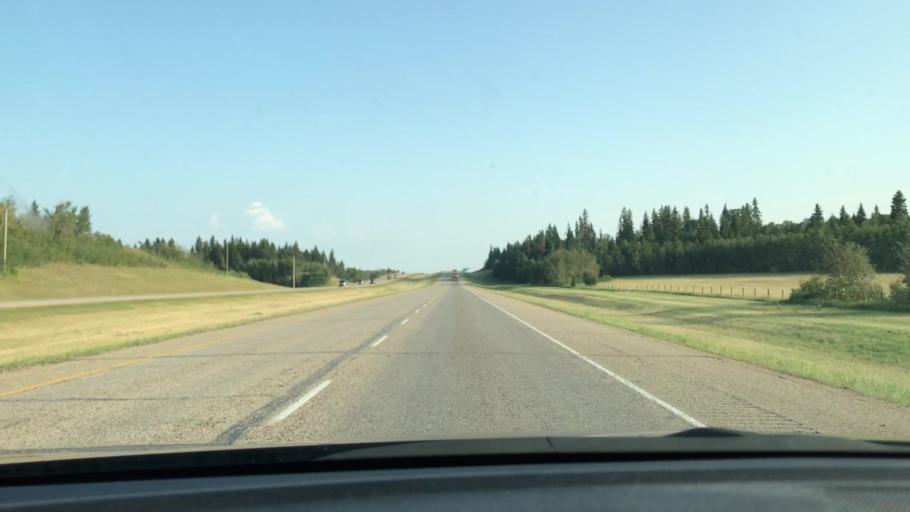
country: CA
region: Alberta
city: Ponoka
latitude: 52.5979
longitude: -113.6635
